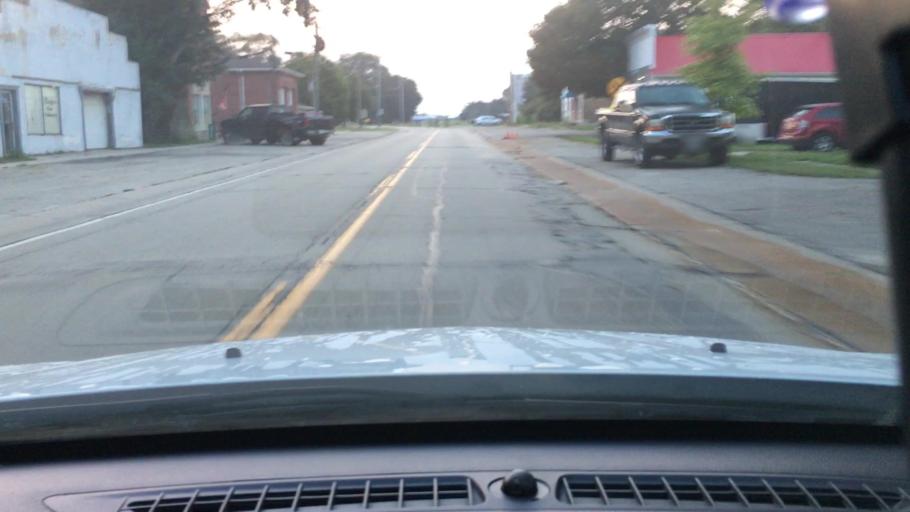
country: US
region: Illinois
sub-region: Ogle County
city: Rochelle
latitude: 41.8476
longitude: -89.0207
